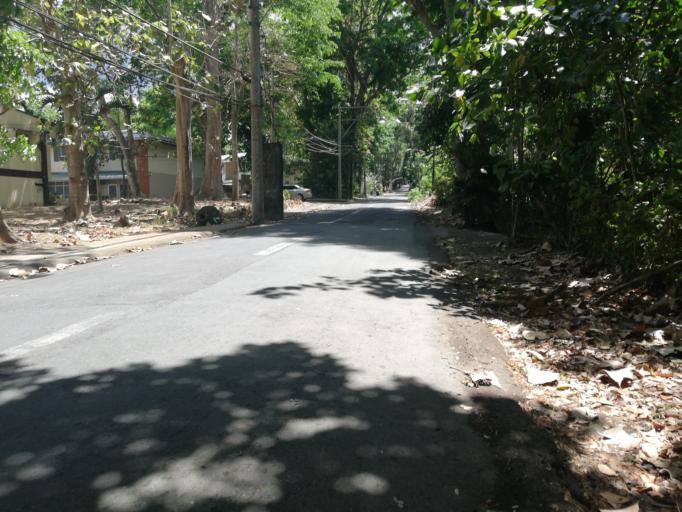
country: PH
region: Calabarzon
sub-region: Province of Laguna
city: Los Banos
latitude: 14.1591
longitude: 121.2375
